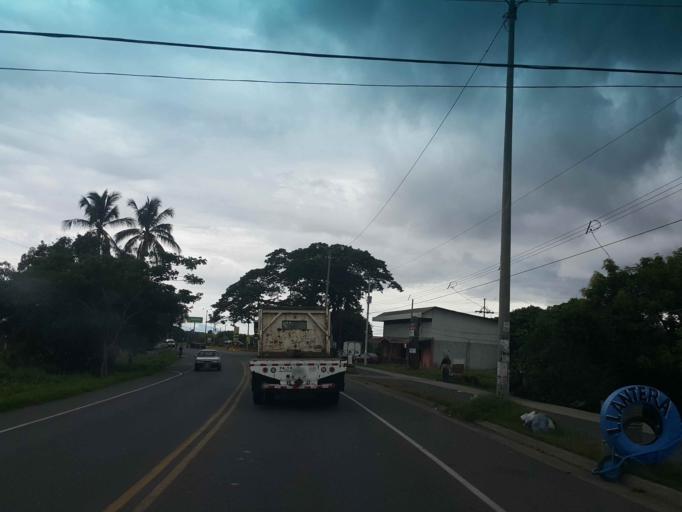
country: CR
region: Puntarenas
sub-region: Canton Central de Puntarenas
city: Chacarita
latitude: 9.9871
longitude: -84.7352
